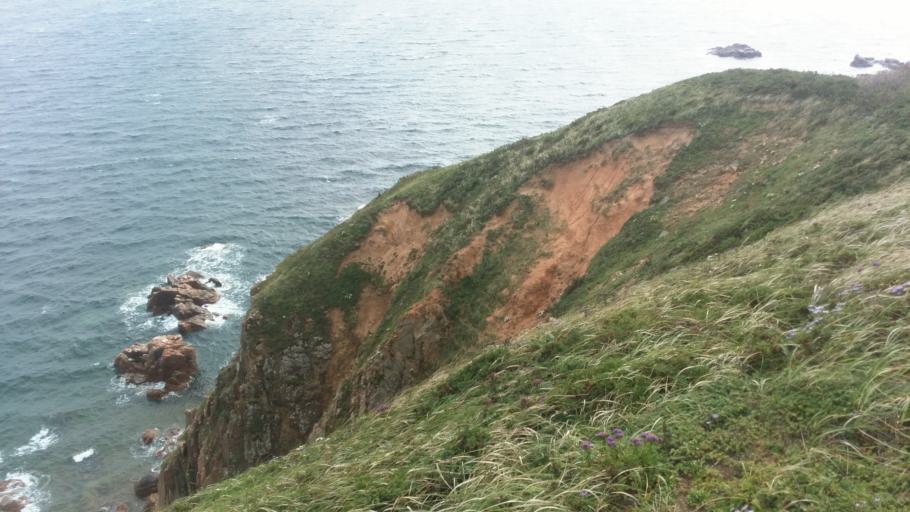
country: RU
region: Primorskiy
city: Popova
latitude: 42.8254
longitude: 131.6171
